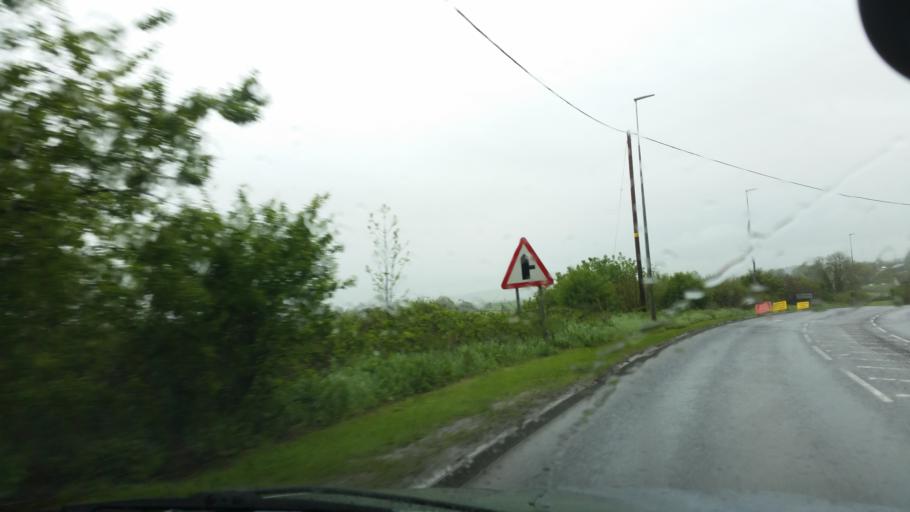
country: GB
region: Northern Ireland
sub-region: Strabane District
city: Strabane
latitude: 54.8418
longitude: -7.4522
